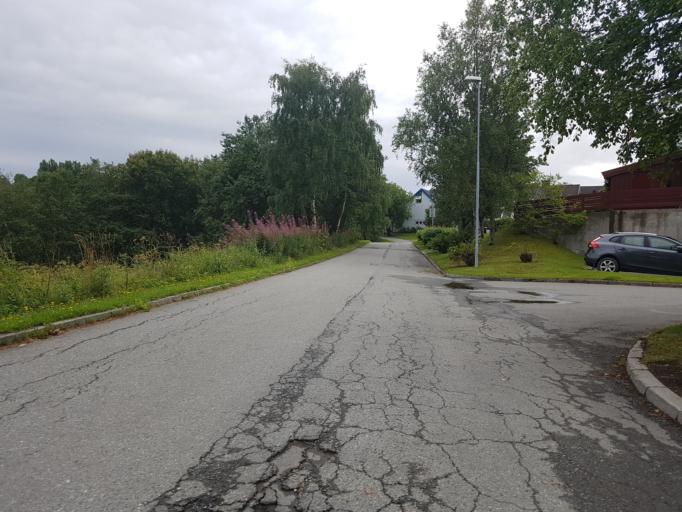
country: NO
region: Sor-Trondelag
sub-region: Trondheim
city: Trondheim
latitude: 63.3858
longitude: 10.4036
